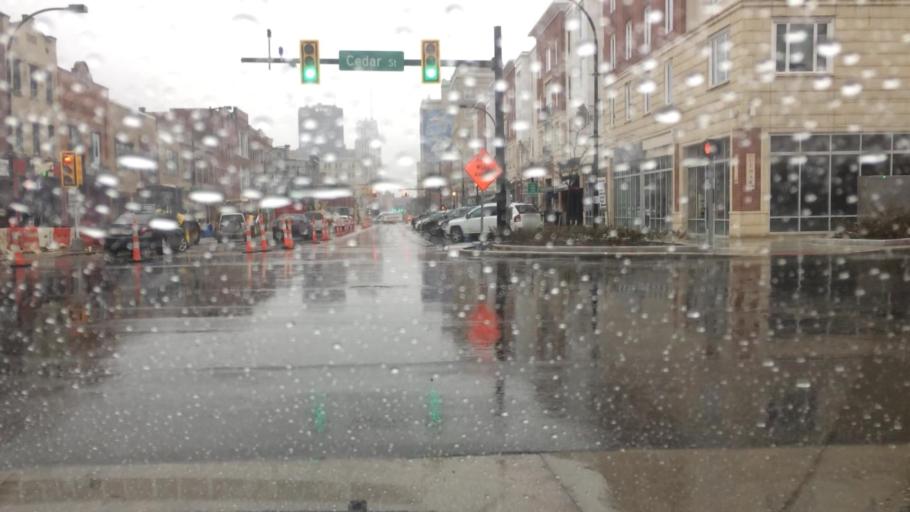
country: US
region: Ohio
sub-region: Summit County
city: Akron
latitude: 41.0754
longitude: -81.5229
